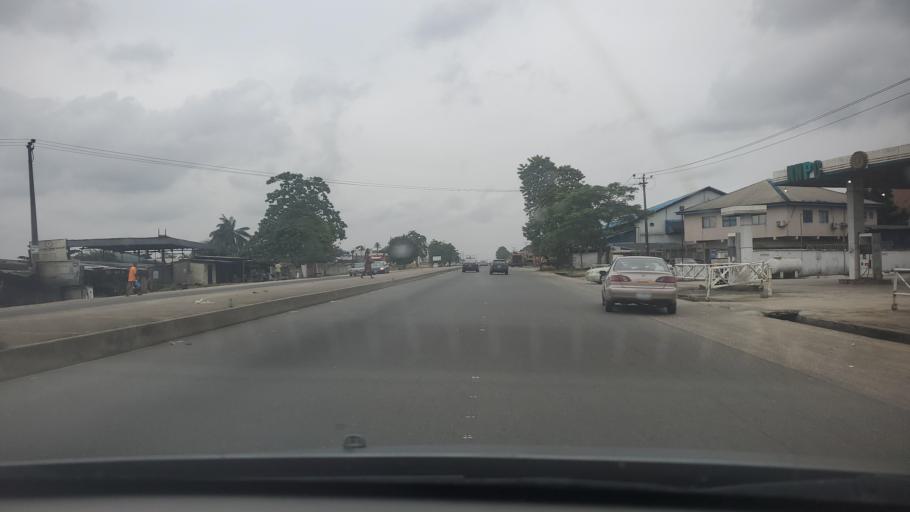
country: NG
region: Rivers
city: Port Harcourt
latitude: 4.8706
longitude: 6.9691
